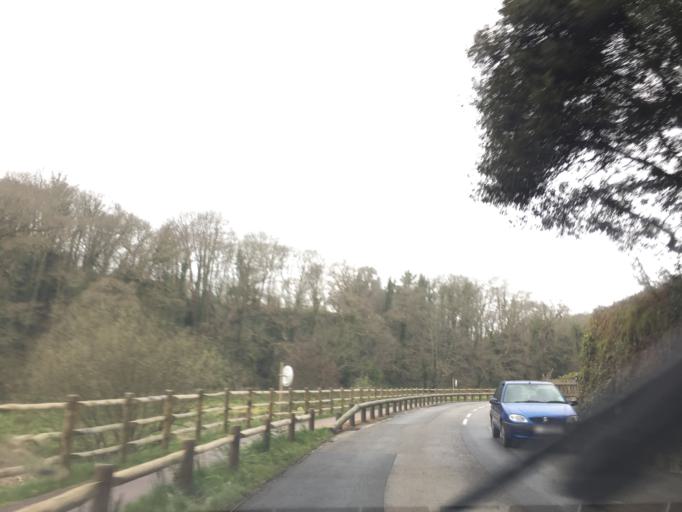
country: JE
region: St Helier
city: Saint Helier
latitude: 49.2062
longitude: -2.1576
